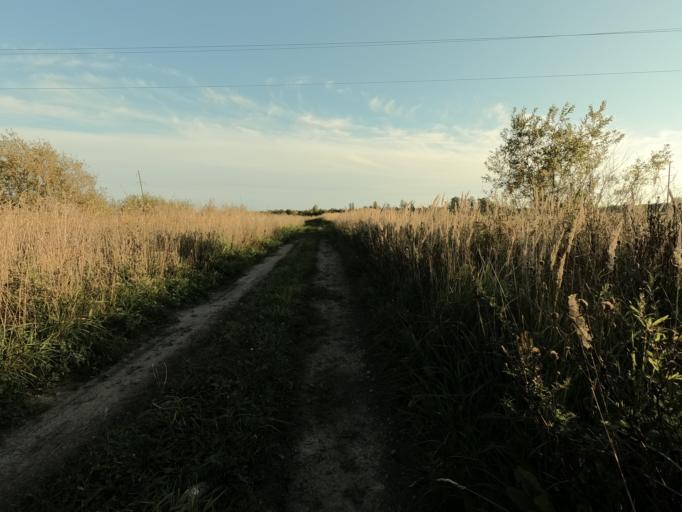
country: RU
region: Leningrad
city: Nikol'skoye
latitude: 59.7000
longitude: 30.7459
